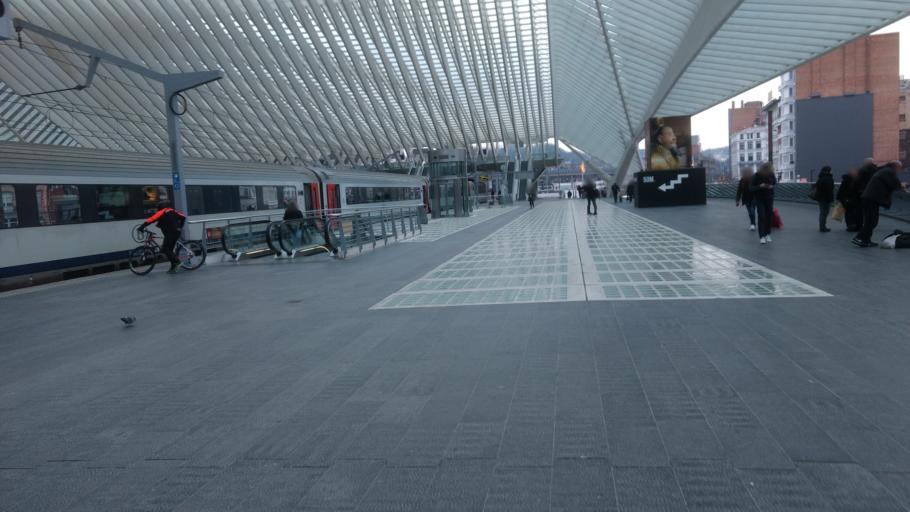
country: BE
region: Wallonia
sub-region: Province de Liege
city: Liege
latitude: 50.6243
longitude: 5.5675
